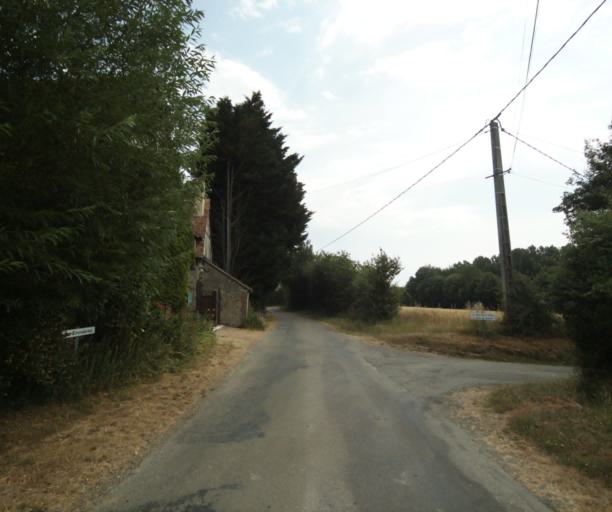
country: FR
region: Centre
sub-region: Departement d'Eure-et-Loir
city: La Bazoche-Gouet
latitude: 48.1839
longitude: 0.9635
